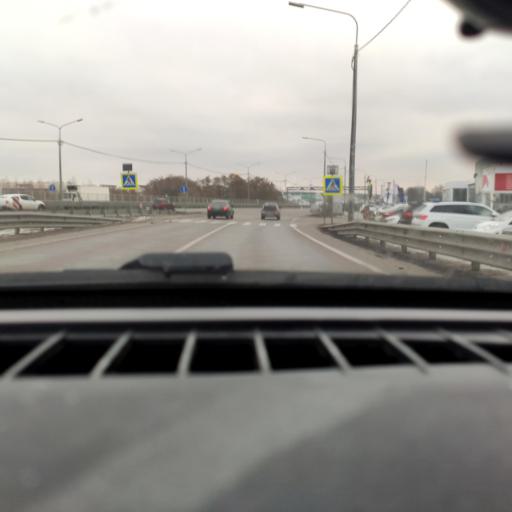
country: RU
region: Voronezj
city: Podgornoye
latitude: 51.7968
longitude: 39.2006
